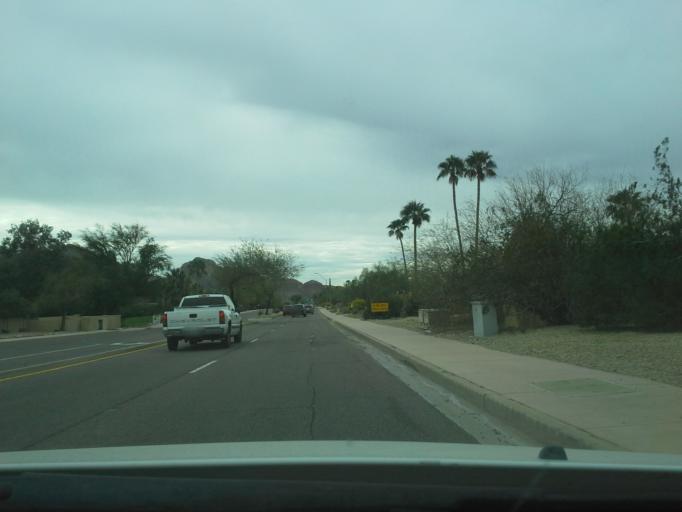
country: US
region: Arizona
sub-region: Maricopa County
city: Paradise Valley
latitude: 33.5484
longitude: -111.9757
